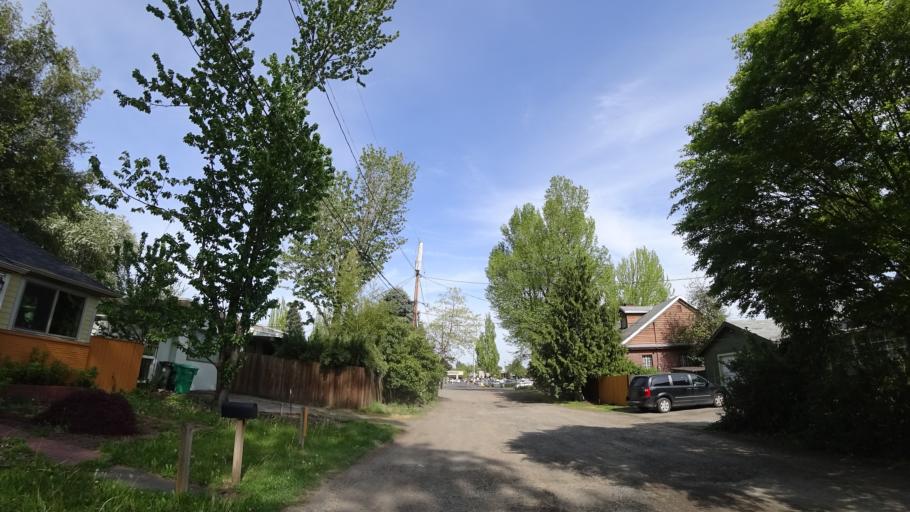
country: US
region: Oregon
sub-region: Clackamas County
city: Milwaukie
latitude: 45.4800
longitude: -122.6193
